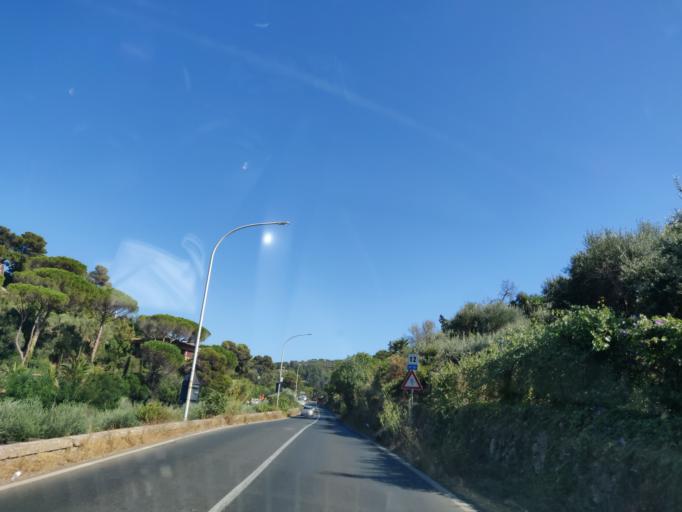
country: IT
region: Tuscany
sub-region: Provincia di Grosseto
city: Monte Argentario
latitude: 42.4366
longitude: 11.1348
